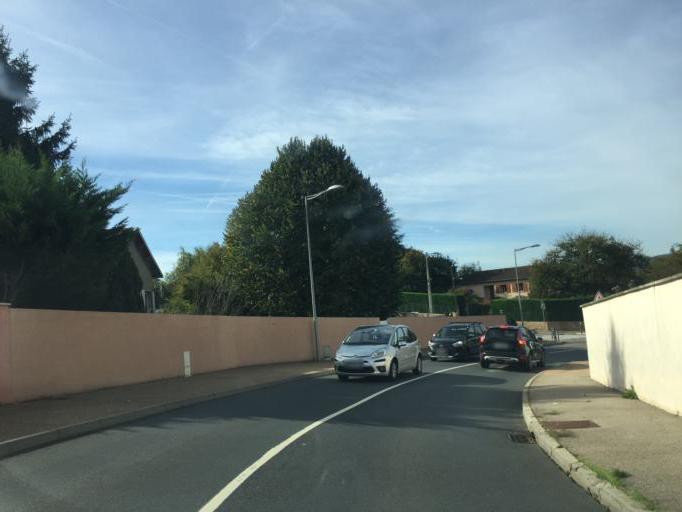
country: FR
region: Rhone-Alpes
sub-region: Departement du Rhone
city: Montanay
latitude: 45.8787
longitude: 4.8599
